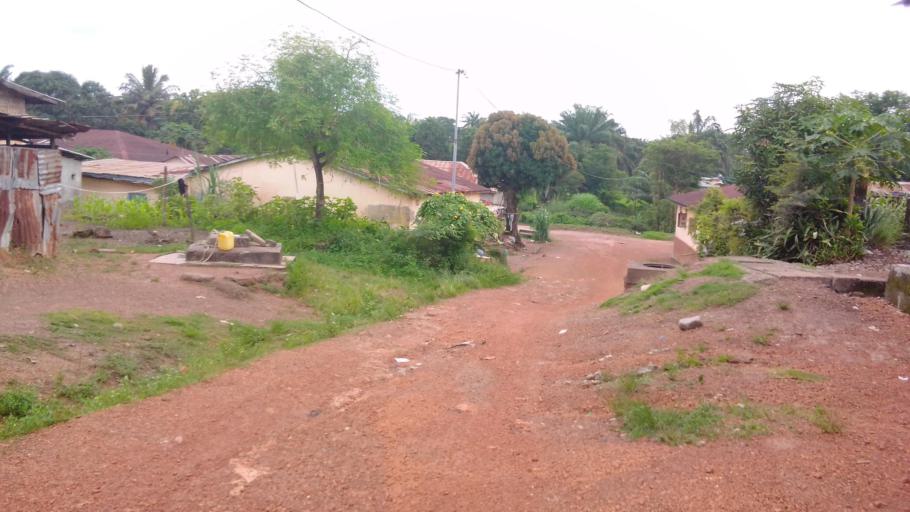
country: SL
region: Northern Province
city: Makeni
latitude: 8.8805
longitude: -12.0421
